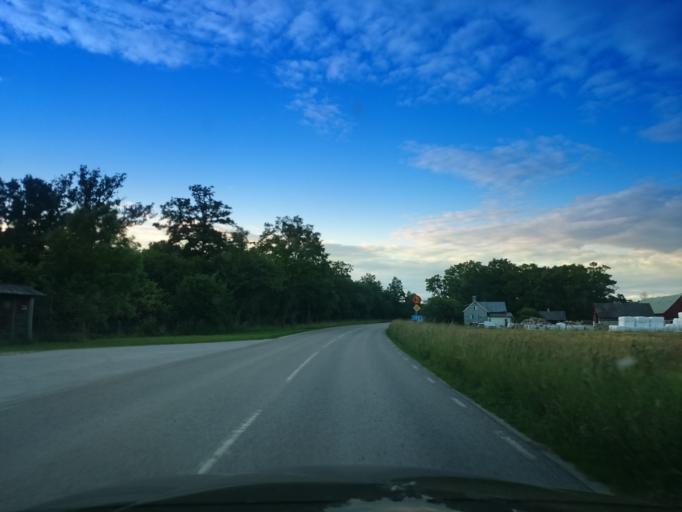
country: SE
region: Gotland
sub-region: Gotland
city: Hemse
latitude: 57.3093
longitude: 18.3800
